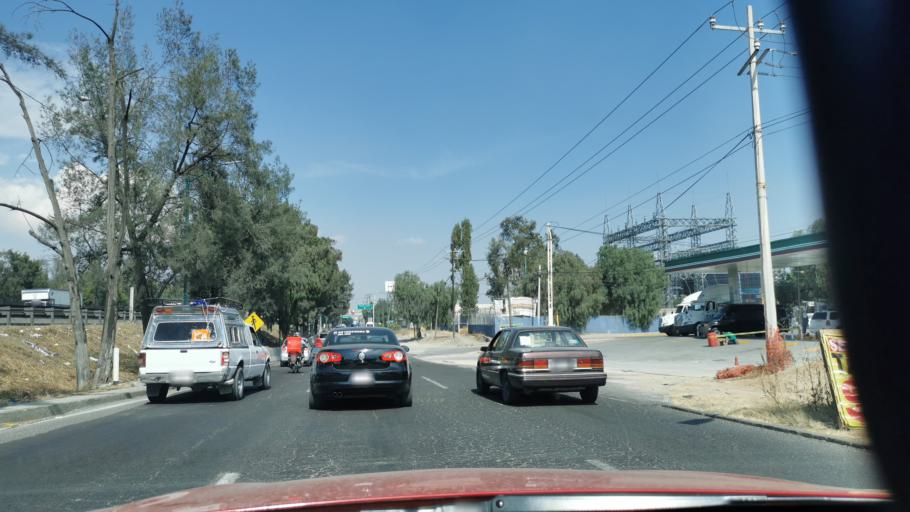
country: MX
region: Mexico
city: Cuautitlan
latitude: 19.6588
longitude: -99.1979
